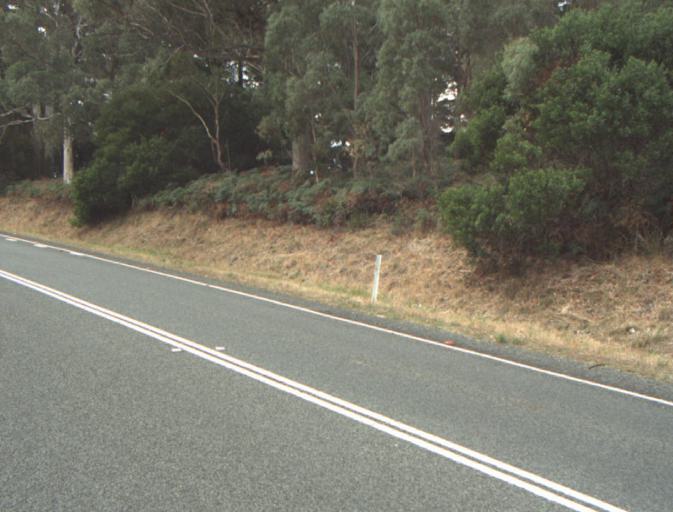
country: AU
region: Tasmania
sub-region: Launceston
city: Mayfield
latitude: -41.2810
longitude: 147.0386
